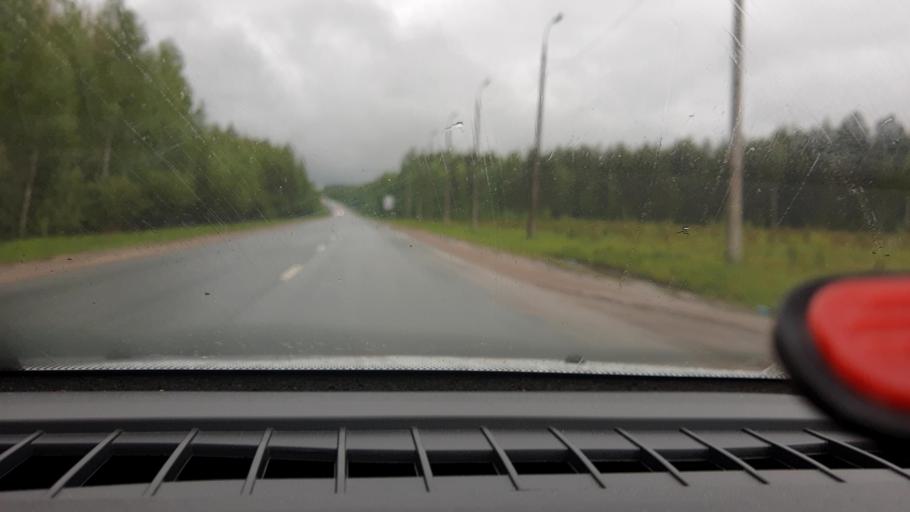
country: RU
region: Nizjnij Novgorod
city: Semenov
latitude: 56.7698
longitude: 44.4150
